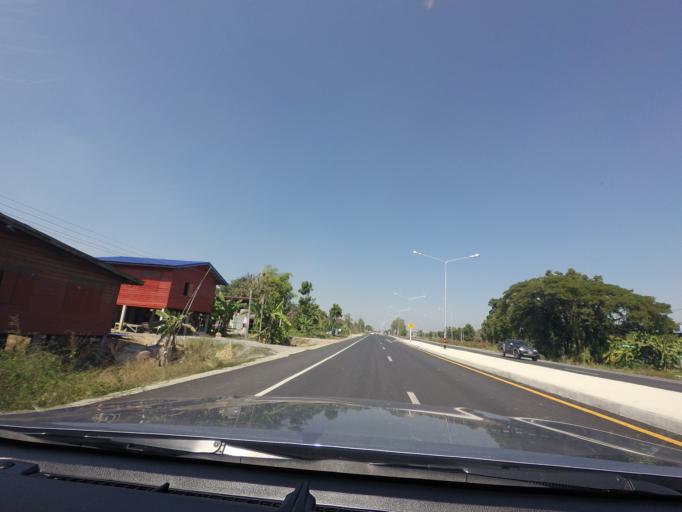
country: TH
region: Sukhothai
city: Ban Na
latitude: 17.0189
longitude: 99.7338
